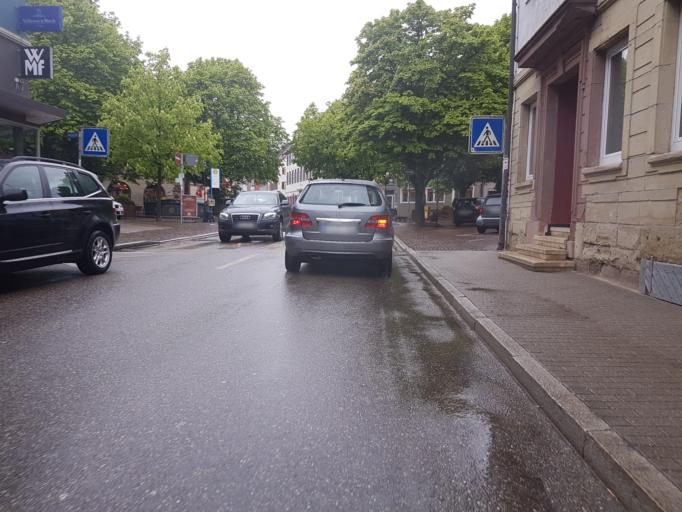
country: DE
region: Baden-Wuerttemberg
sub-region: Freiburg Region
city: Sulz am Neckar
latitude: 48.3623
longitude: 8.6317
